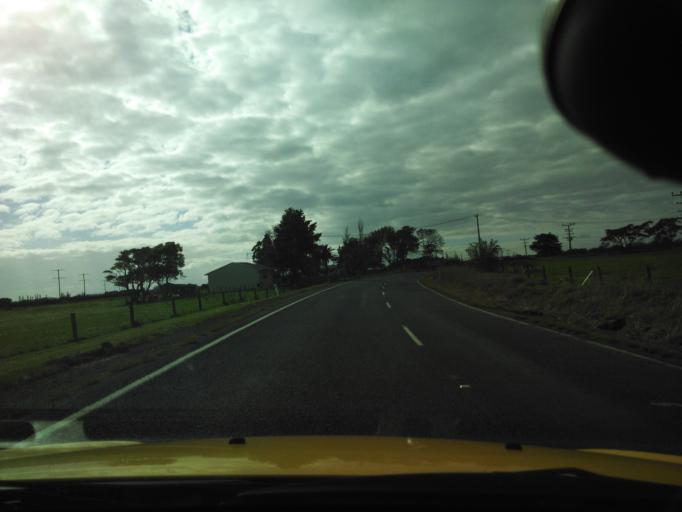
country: NZ
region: Waikato
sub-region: Waikato District
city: Te Kauwhata
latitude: -37.4782
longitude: 175.1436
